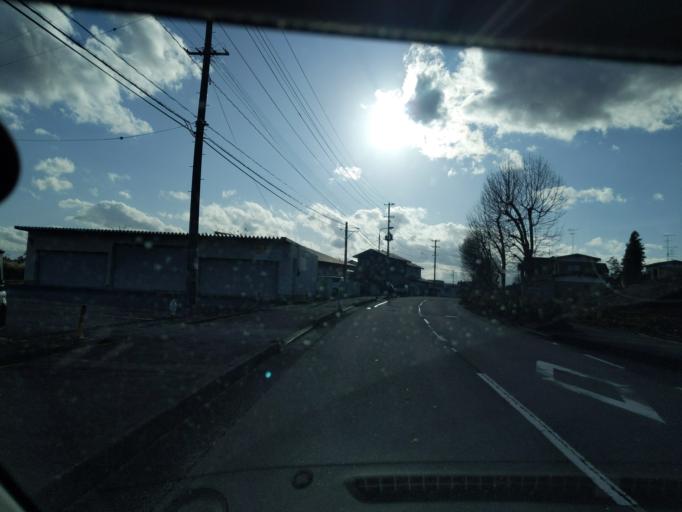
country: JP
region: Iwate
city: Mizusawa
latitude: 39.1204
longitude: 141.1101
